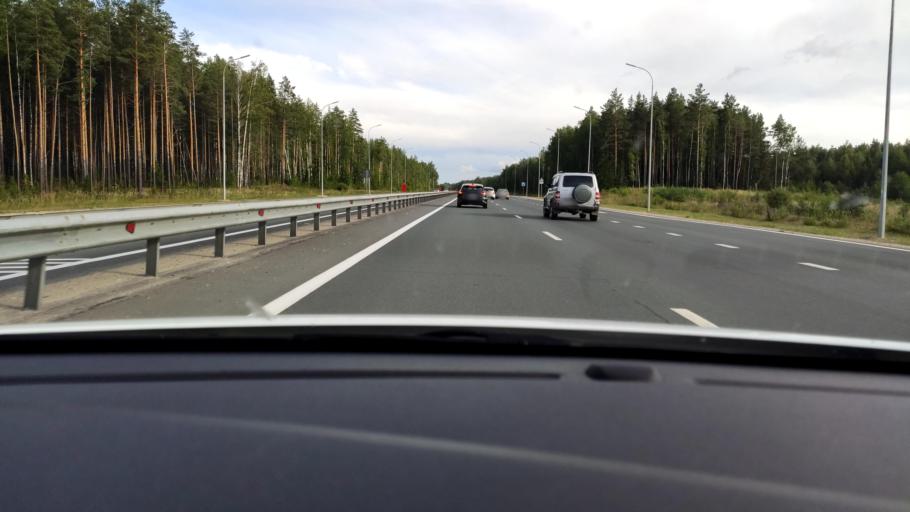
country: RU
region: Mariy-El
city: Surok
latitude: 56.5166
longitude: 48.0155
